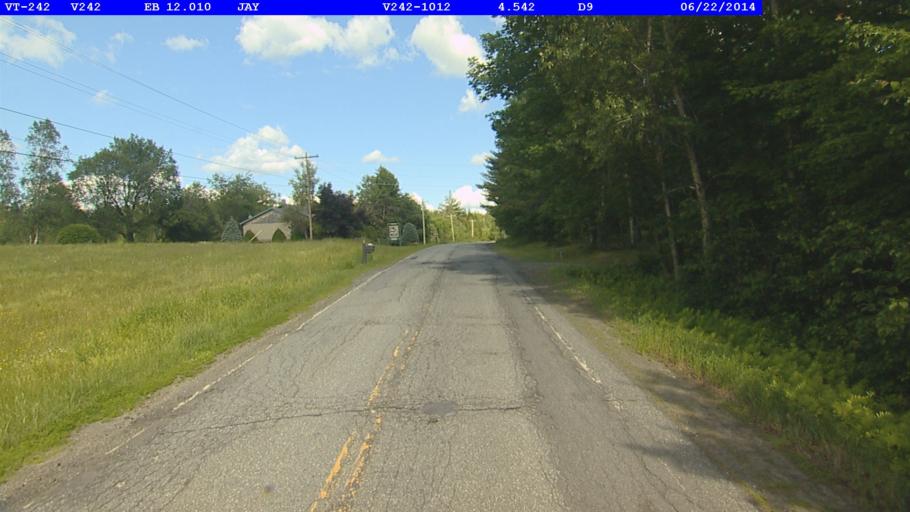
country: US
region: Vermont
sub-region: Orleans County
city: Newport
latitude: 44.9491
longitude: -72.4286
